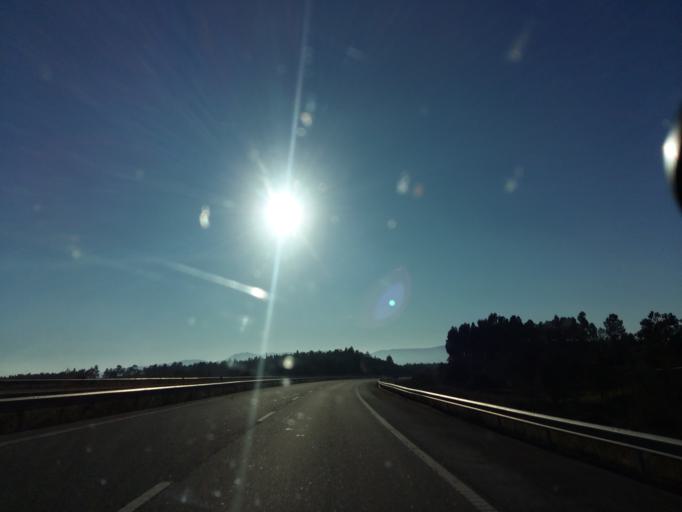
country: PT
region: Castelo Branco
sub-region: Castelo Branco
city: Castelo Branco
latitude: 39.7439
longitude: -7.6355
